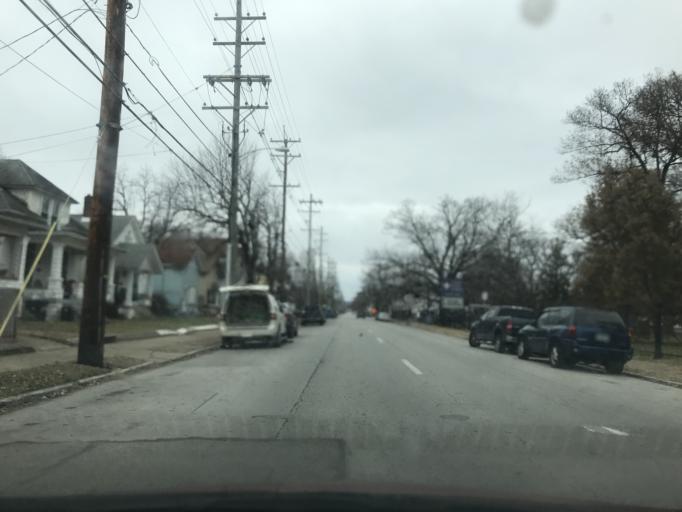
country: US
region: Kentucky
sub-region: Jefferson County
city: Louisville
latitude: 38.2690
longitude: -85.7843
